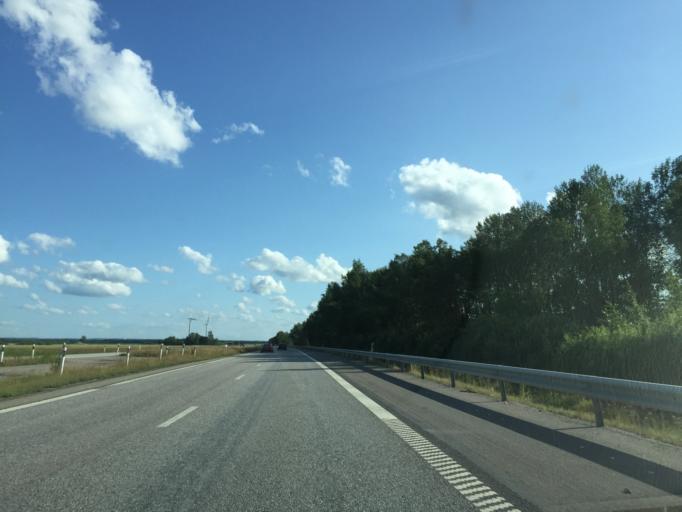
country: SE
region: OErebro
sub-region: Kumla Kommun
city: Kumla
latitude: 59.2065
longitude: 15.1279
